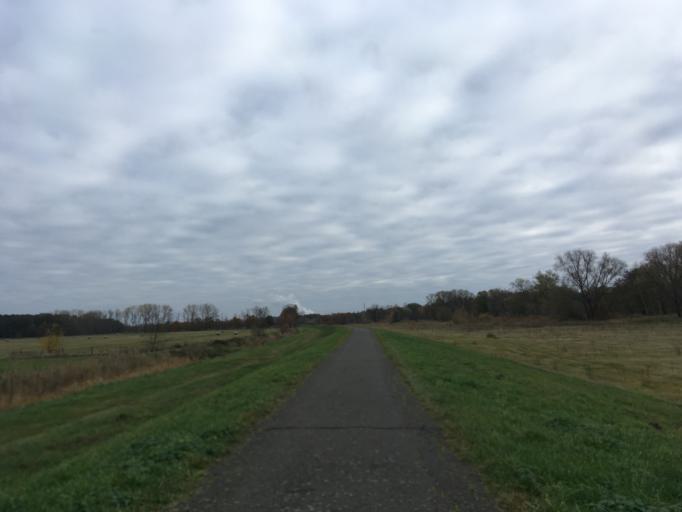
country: DE
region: Brandenburg
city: Briesen
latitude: 51.8460
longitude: 14.2740
